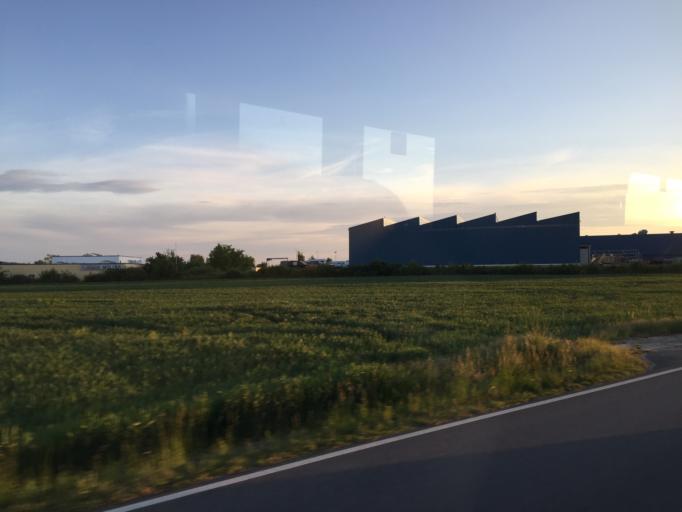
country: DE
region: Saxony
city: Markersdorf
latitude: 51.1459
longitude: 14.8711
